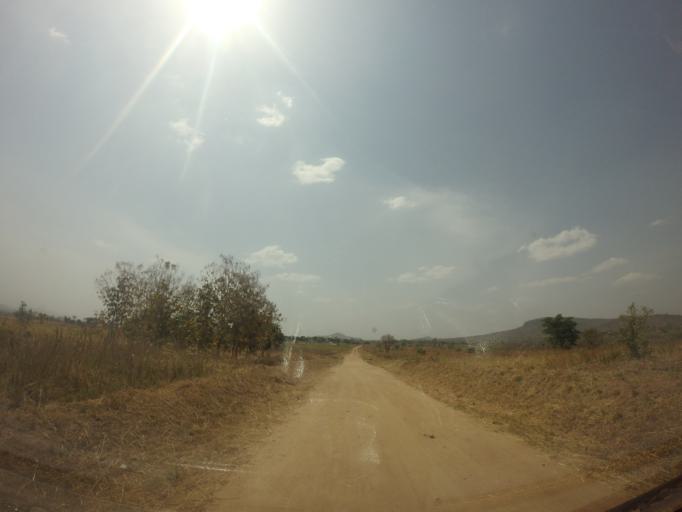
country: UG
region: Northern Region
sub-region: Arua District
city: Arua
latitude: 2.9127
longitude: 31.0444
